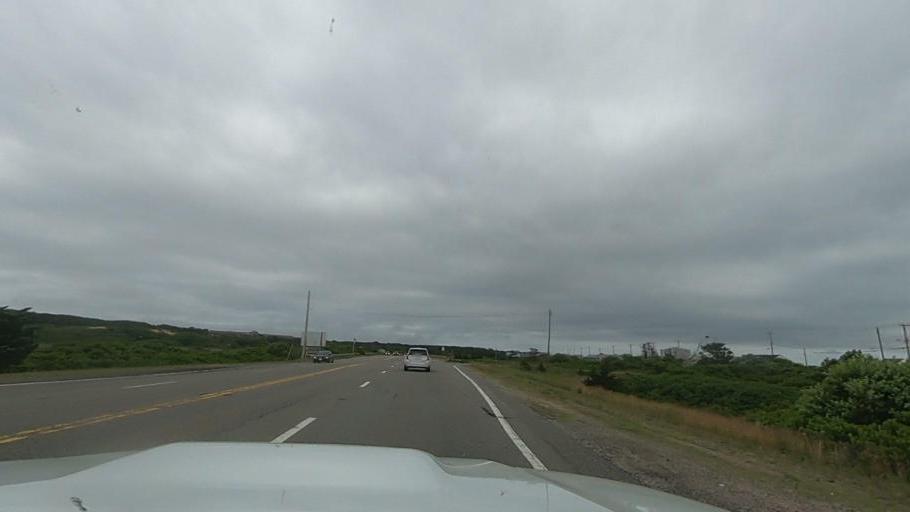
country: US
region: Massachusetts
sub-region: Barnstable County
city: Provincetown
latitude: 42.0516
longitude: -70.1197
